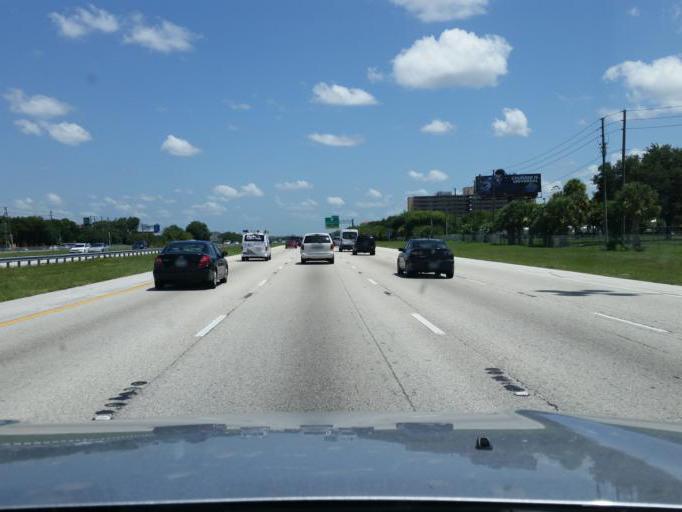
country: US
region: Florida
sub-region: Orange County
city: Doctor Phillips
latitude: 28.4274
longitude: -81.4741
